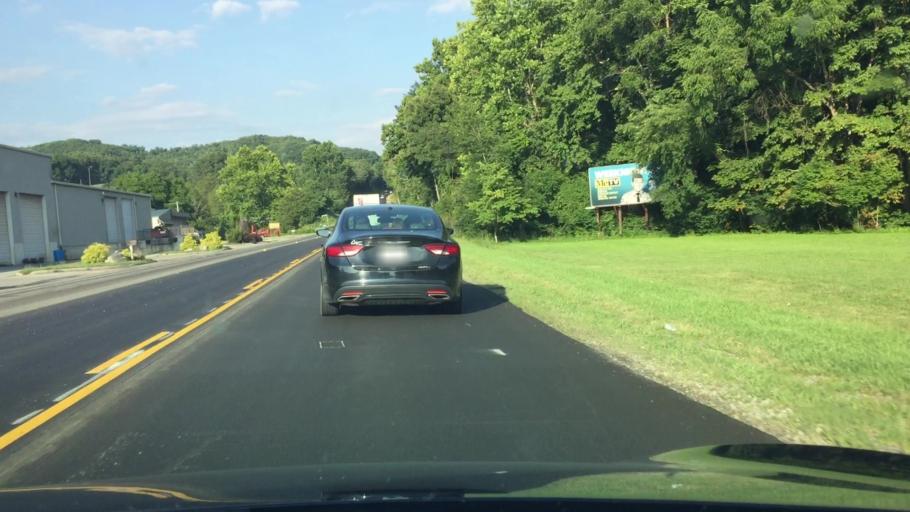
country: US
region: Virginia
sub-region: Montgomery County
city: Prices Fork
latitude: 37.1306
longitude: -80.4887
